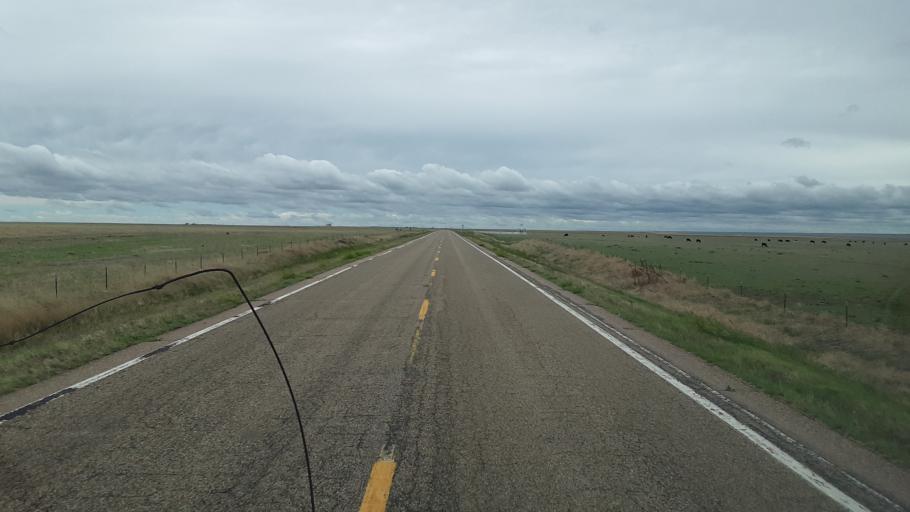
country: US
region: Colorado
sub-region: Lincoln County
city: Limon
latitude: 38.8522
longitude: -103.7843
